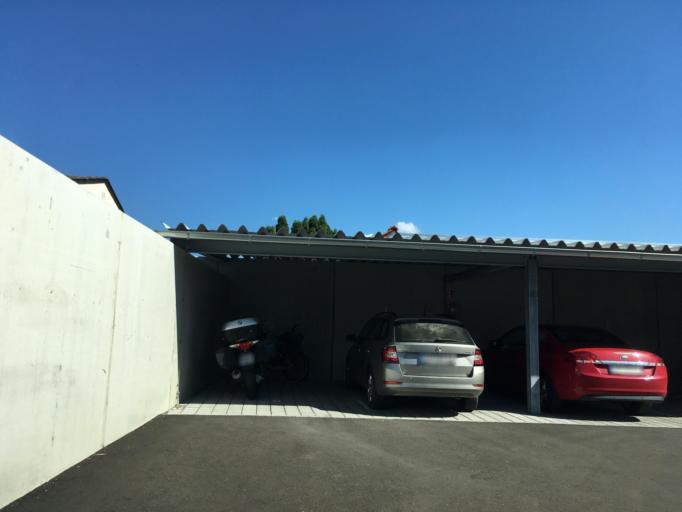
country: AT
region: Styria
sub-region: Politischer Bezirk Leoben
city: Trofaiach
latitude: 47.4235
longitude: 15.0118
